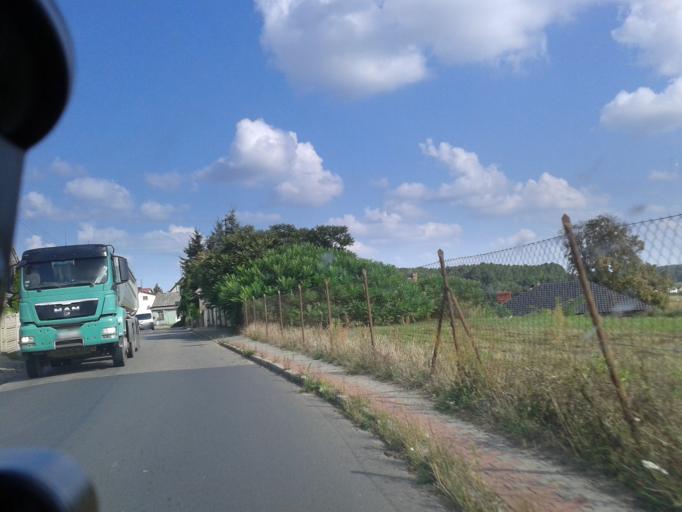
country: PL
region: Greater Poland Voivodeship
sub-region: Powiat szamotulski
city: Obrzycko
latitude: 52.7132
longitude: 16.5307
